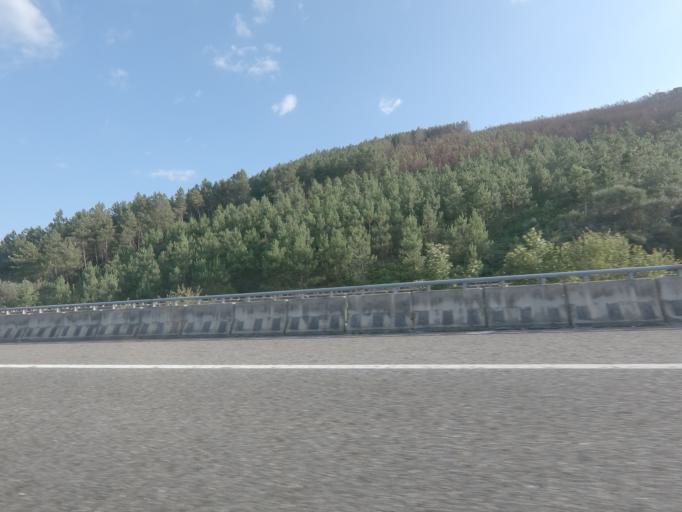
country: ES
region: Galicia
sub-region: Provincia de Ourense
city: Verin
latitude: 41.9200
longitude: -7.4566
